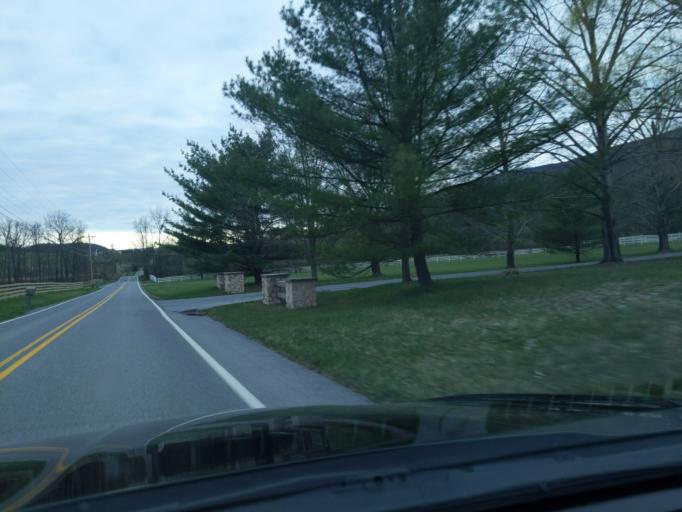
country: US
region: Pennsylvania
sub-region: Blair County
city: Greenwood
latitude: 40.4839
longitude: -78.3154
